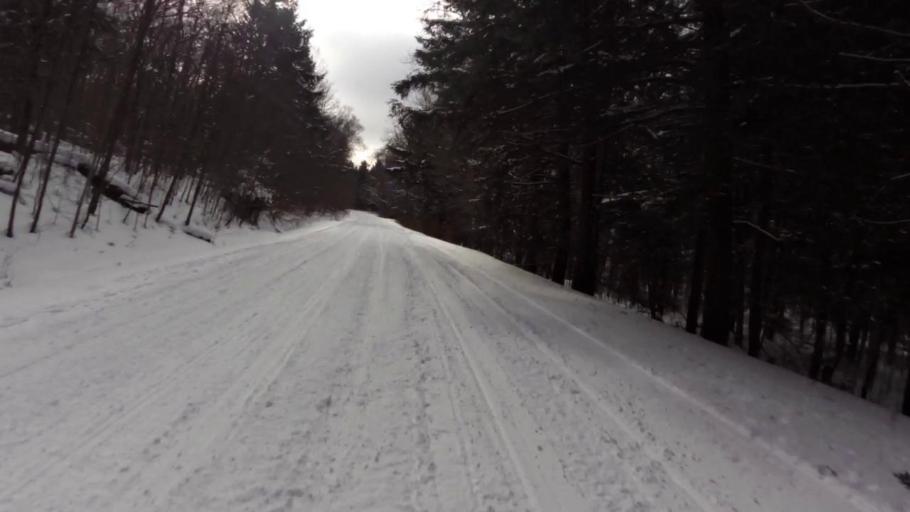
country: US
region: New York
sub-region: Cattaraugus County
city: Salamanca
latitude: 42.0740
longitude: -78.7538
